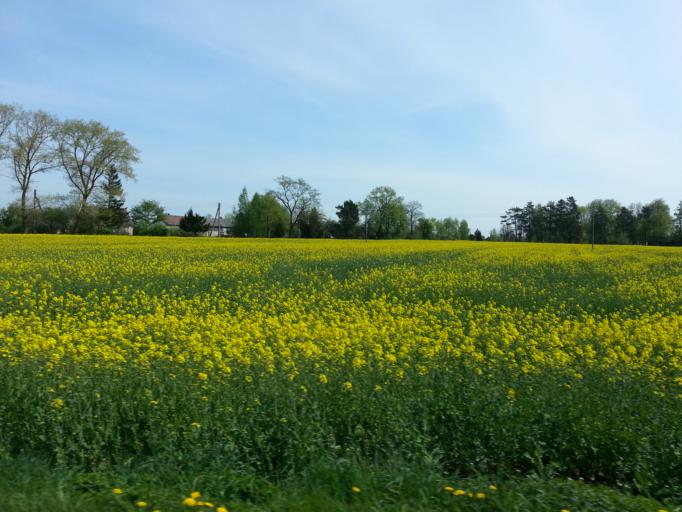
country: LT
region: Panevezys
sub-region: Panevezys City
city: Panevezys
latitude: 55.8653
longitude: 24.2428
